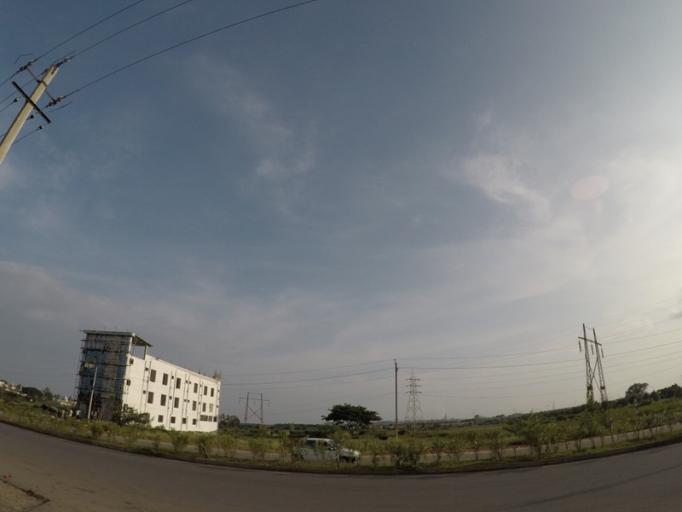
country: IN
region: Karnataka
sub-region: Chikmagalur
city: Chikmagalur
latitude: 13.3083
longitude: 75.7906
